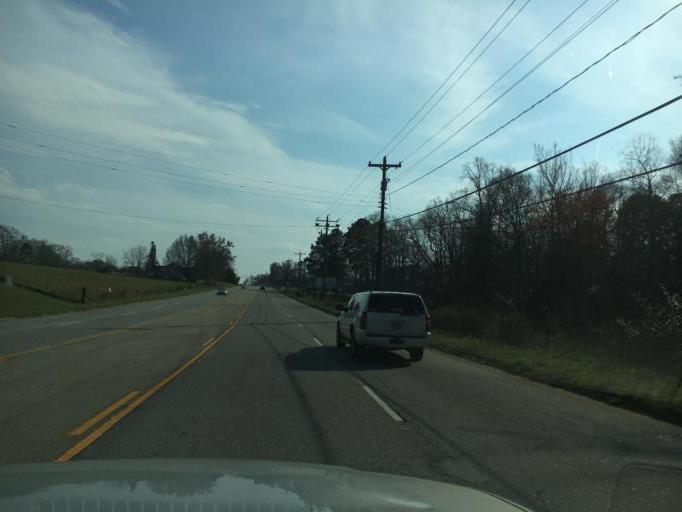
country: US
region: South Carolina
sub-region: Spartanburg County
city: Mayo
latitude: 35.0362
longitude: -81.8945
